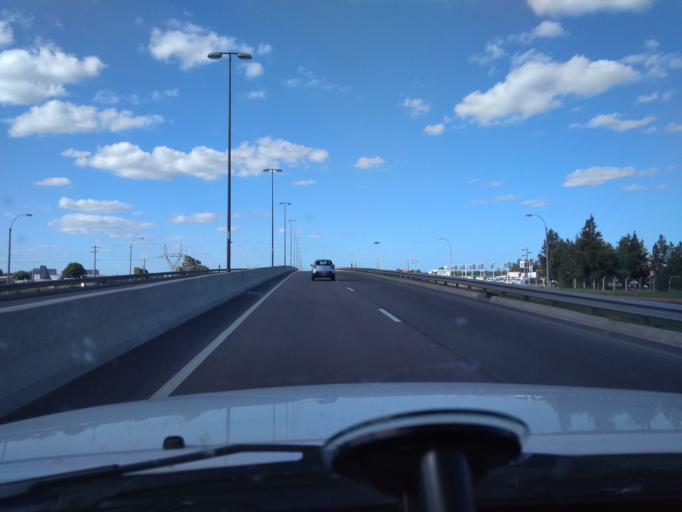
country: UY
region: Canelones
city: Las Piedras
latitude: -34.7232
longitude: -56.2466
